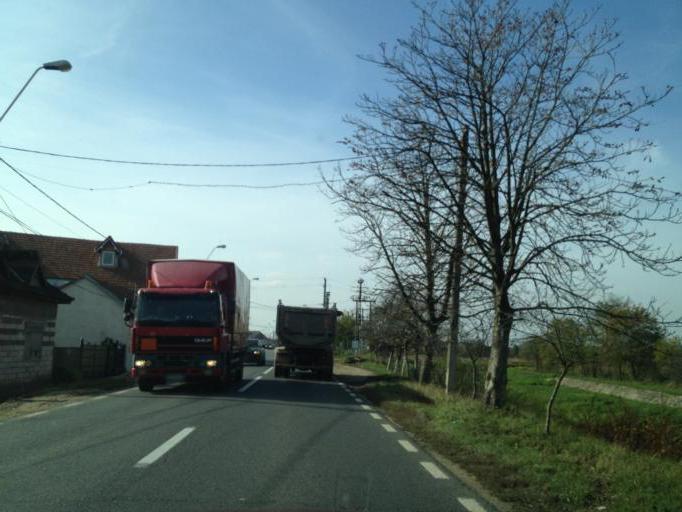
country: RO
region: Timis
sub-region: Comuna Faget
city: Faget
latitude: 45.8571
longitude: 22.1873
